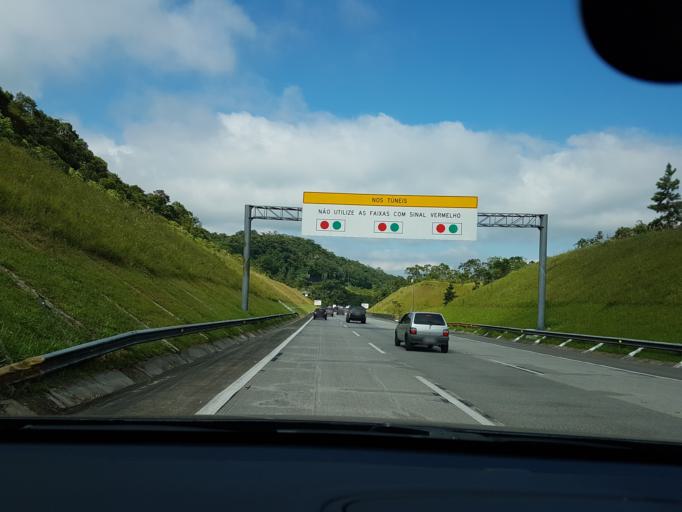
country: BR
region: Sao Paulo
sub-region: Cubatao
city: Cubatao
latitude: -23.9266
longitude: -46.5433
